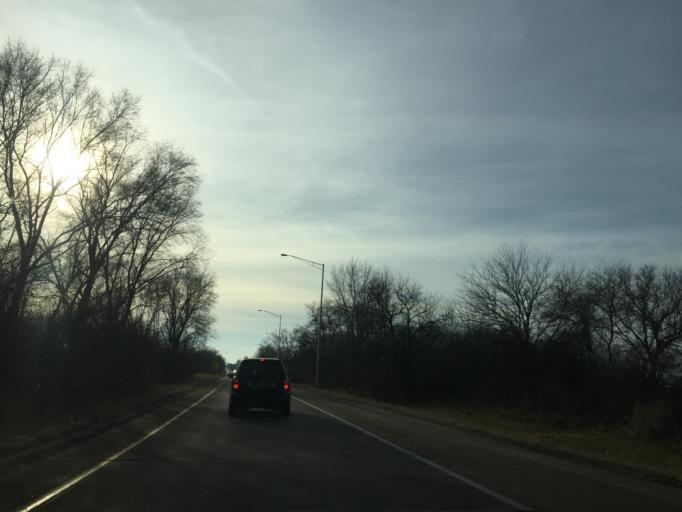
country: US
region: Illinois
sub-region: Will County
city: Plainfield
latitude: 41.6351
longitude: -88.1638
